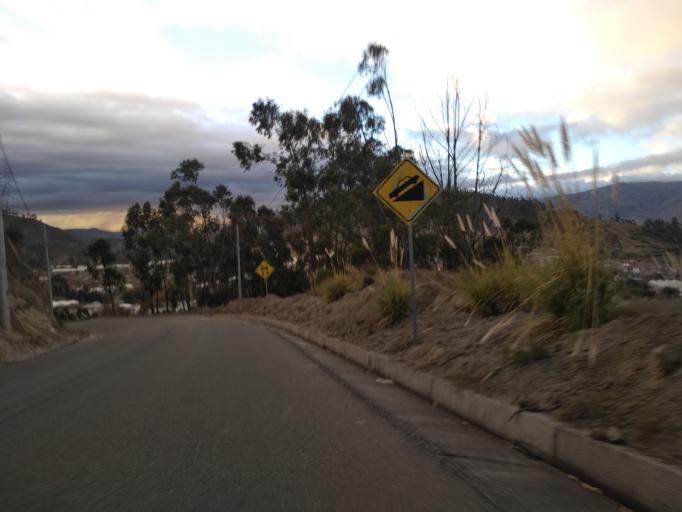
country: EC
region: Chimborazo
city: Riobamba
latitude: -1.6862
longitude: -78.6819
